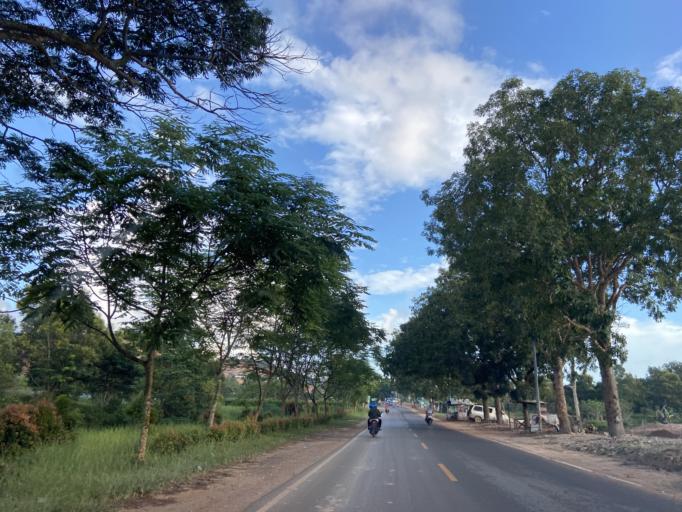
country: SG
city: Singapore
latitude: 1.0244
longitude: 104.0102
